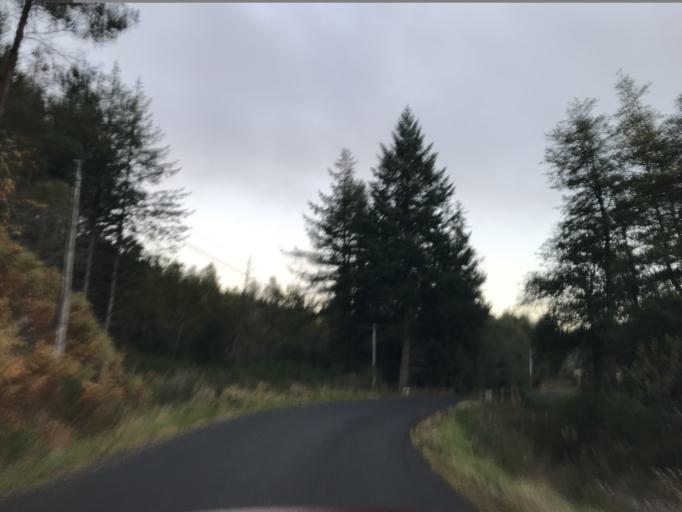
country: FR
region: Auvergne
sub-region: Departement du Puy-de-Dome
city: Celles-sur-Durolle
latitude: 45.7884
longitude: 3.6731
